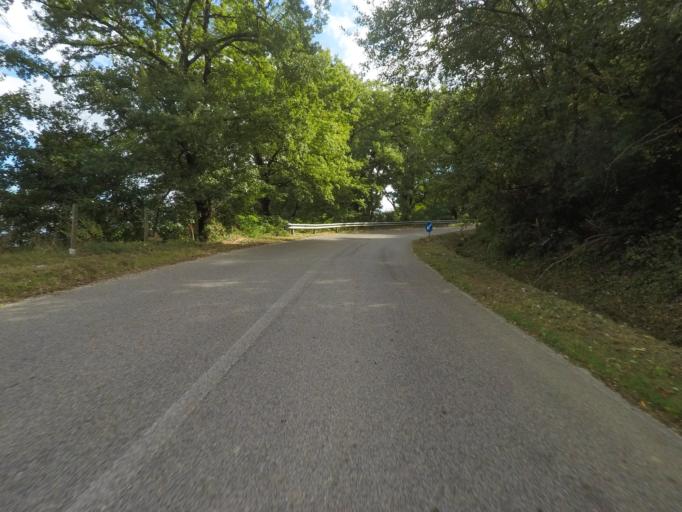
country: IT
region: Tuscany
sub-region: Provincia di Siena
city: Torrita di Siena
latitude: 43.1545
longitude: 11.7773
